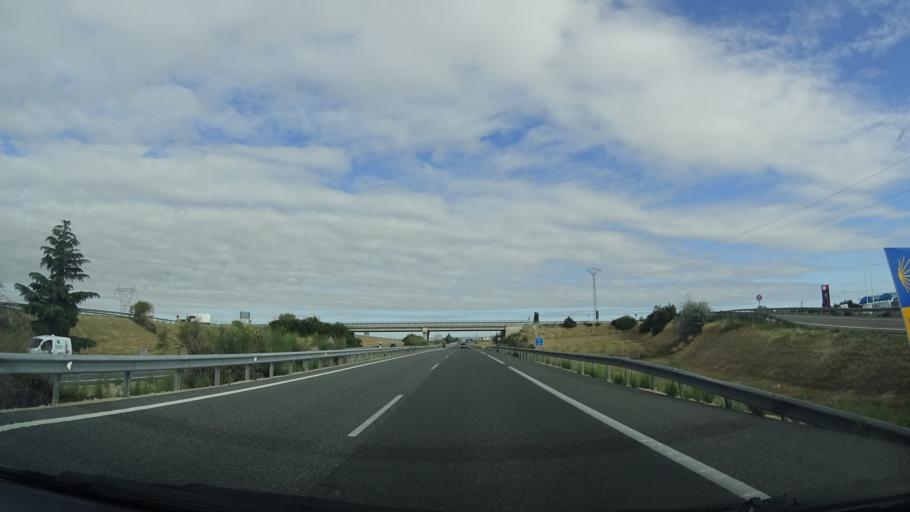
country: ES
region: Castille and Leon
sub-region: Provincia de Valladolid
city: San Vicente del Palacio
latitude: 41.2205
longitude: -4.8426
